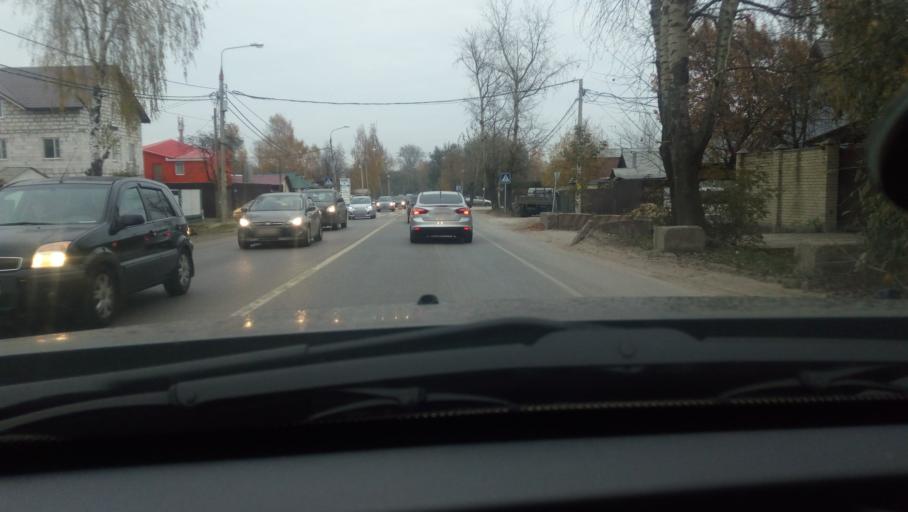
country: RU
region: Moskovskaya
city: Saltykovka
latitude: 55.7525
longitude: 37.9008
